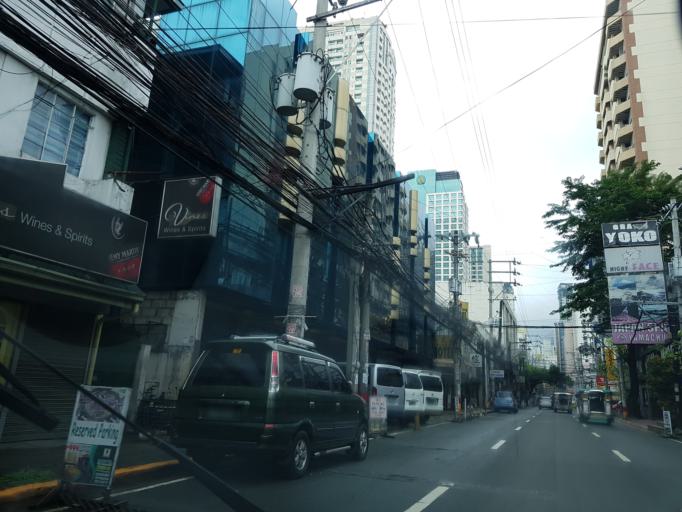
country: PH
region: Metro Manila
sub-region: City of Manila
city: Port Area
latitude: 14.5701
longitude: 120.9846
